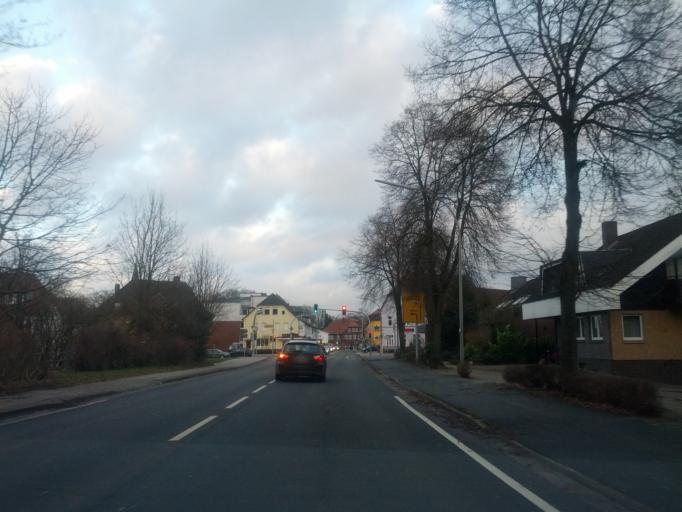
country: DE
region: Lower Saxony
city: Scheessel
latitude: 53.1672
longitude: 9.4803
